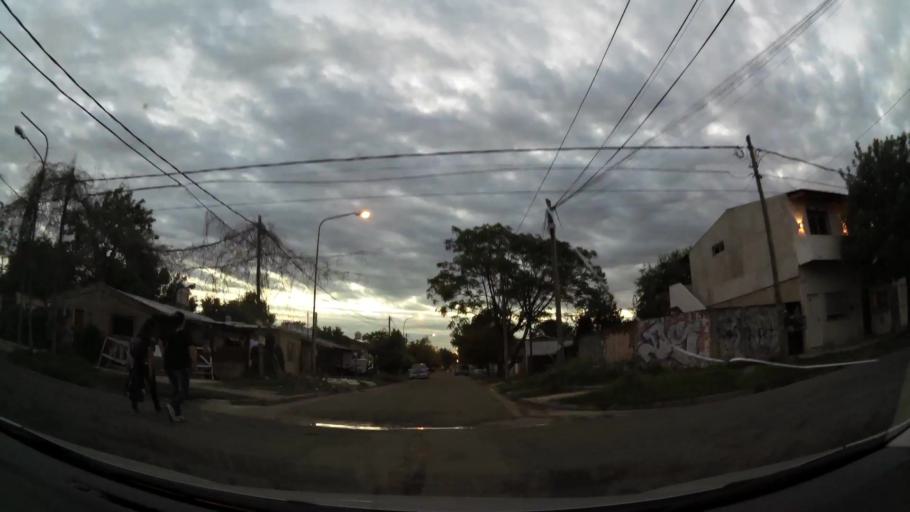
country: AR
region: Buenos Aires
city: Santa Catalina - Dique Lujan
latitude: -34.4155
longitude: -58.6891
